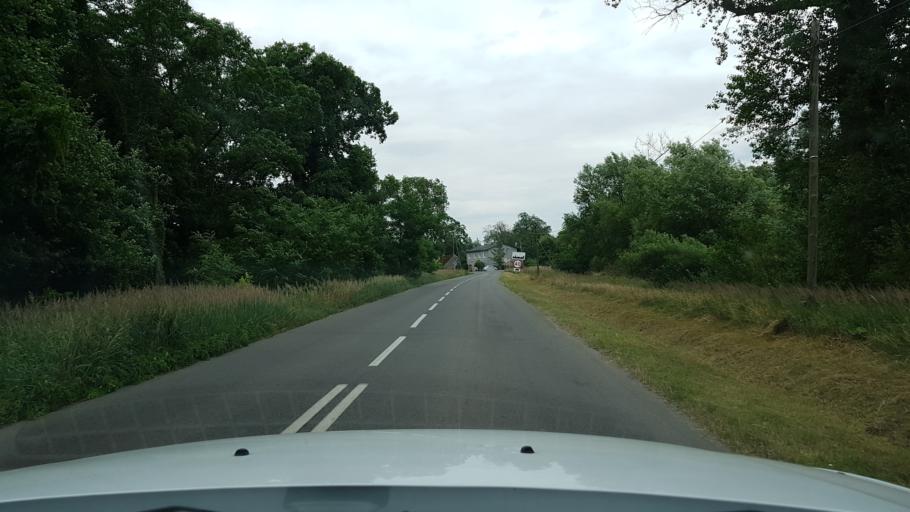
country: DE
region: Brandenburg
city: Manschnow
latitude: 52.6258
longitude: 14.5750
